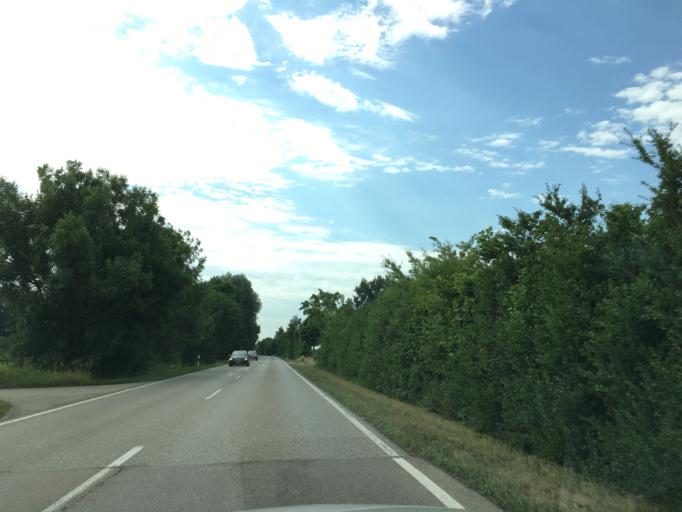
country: DE
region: Bavaria
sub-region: Upper Bavaria
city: Worth
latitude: 48.2577
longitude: 11.9263
